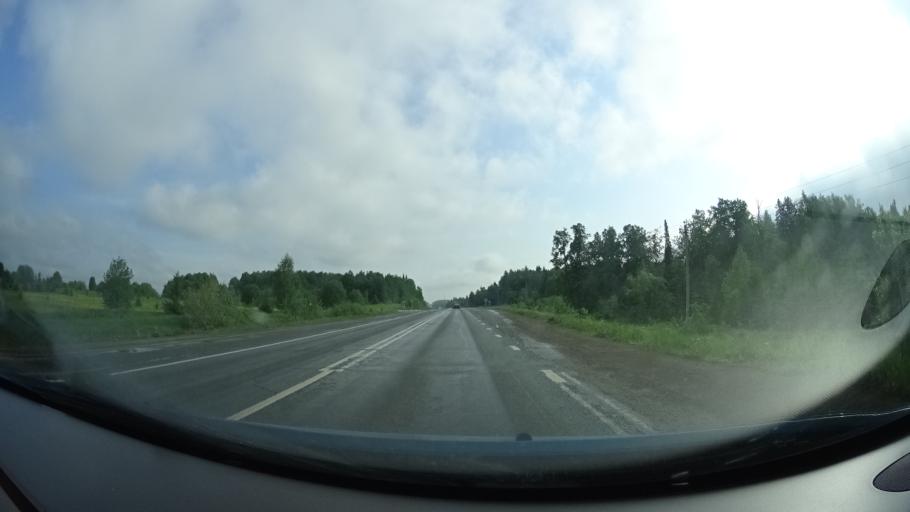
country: RU
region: Perm
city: Kultayevo
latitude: 57.8222
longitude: 55.8041
